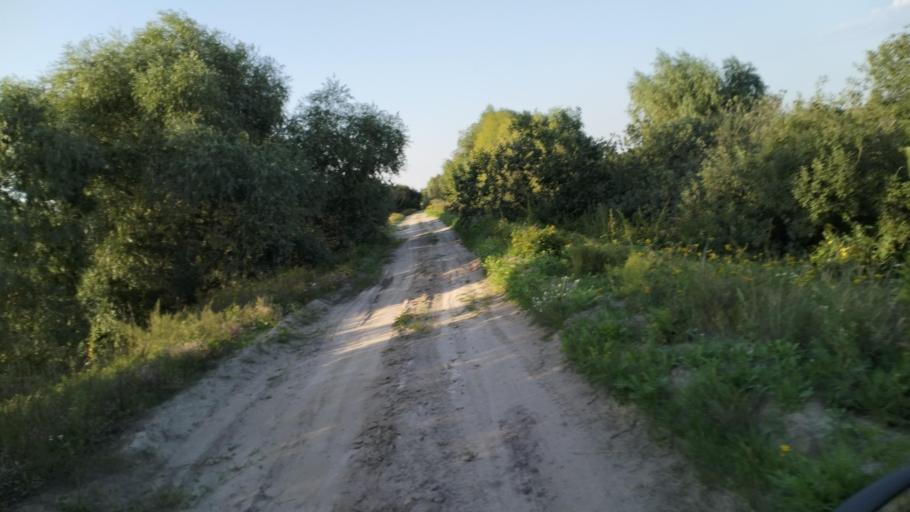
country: BY
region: Brest
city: Davyd-Haradok
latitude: 52.0269
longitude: 27.1945
